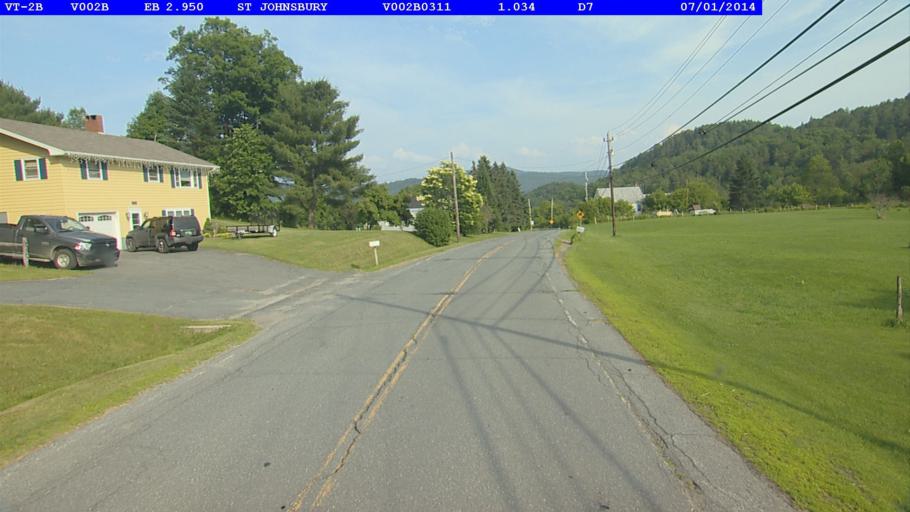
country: US
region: Vermont
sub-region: Caledonia County
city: St Johnsbury
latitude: 44.4232
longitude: -72.0379
